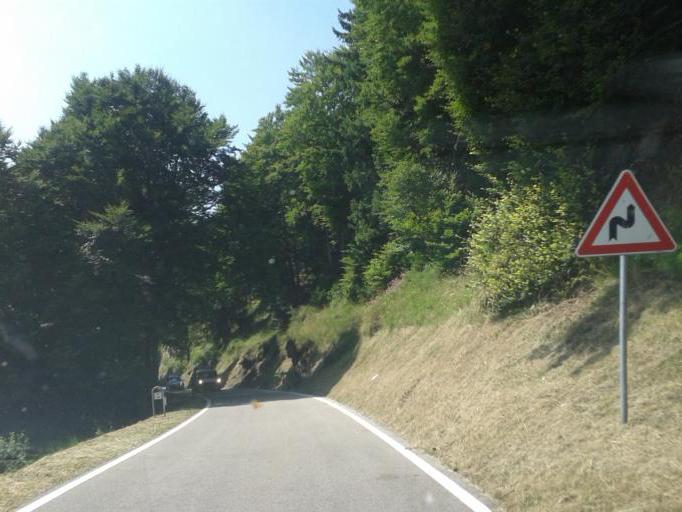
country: IT
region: Trentino-Alto Adige
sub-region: Provincia di Trento
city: Avio
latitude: 45.7838
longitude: 10.9057
